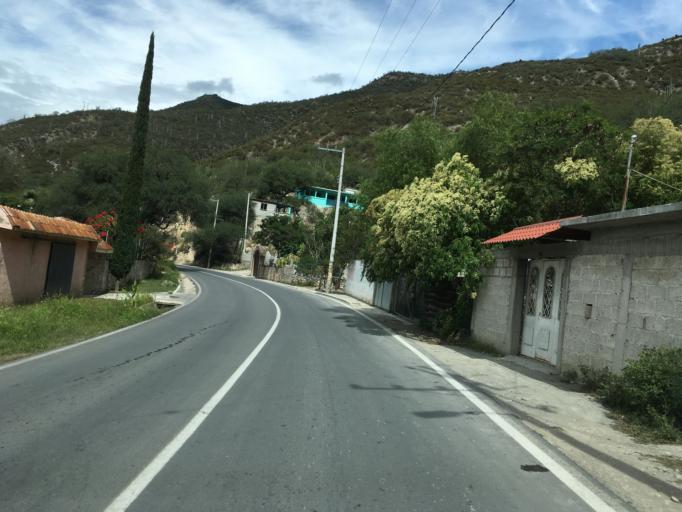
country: MX
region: Hidalgo
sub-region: San Agustin Metzquititlan
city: Mezquititlan
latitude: 20.5039
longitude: -98.7003
